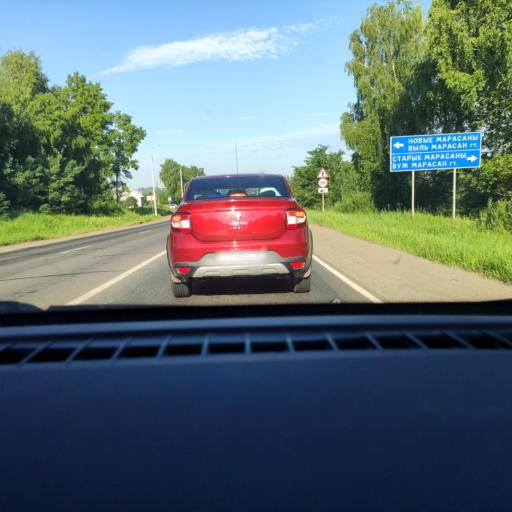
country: RU
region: Udmurtiya
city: Khokhryaki
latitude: 56.9144
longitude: 53.3995
